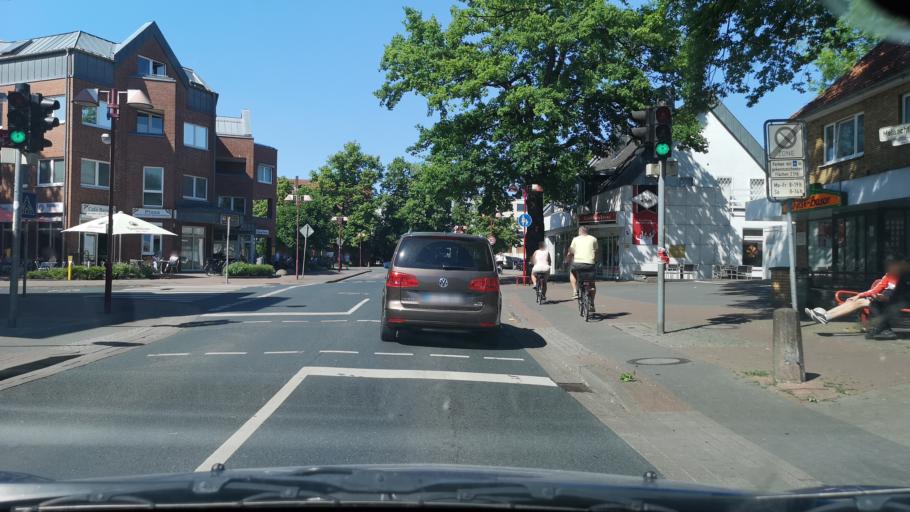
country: DE
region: Lower Saxony
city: Garbsen-Mitte
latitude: 52.4362
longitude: 9.6116
